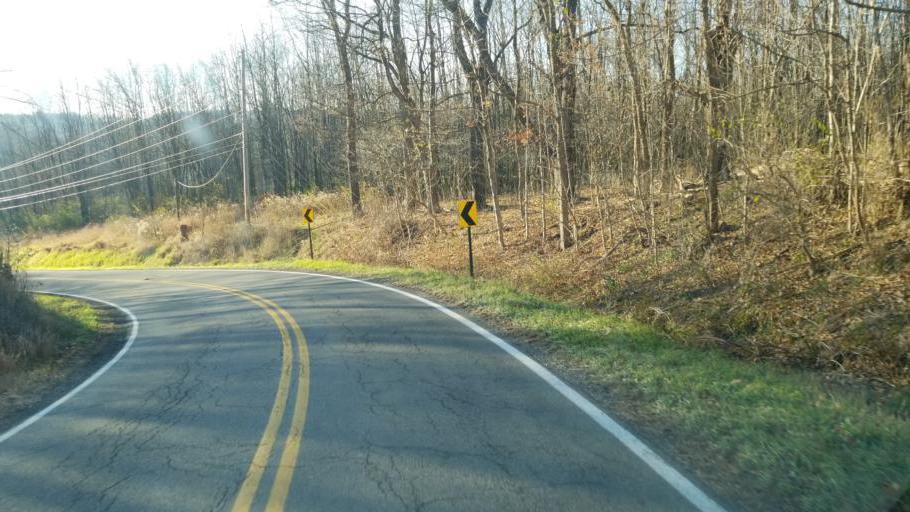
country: US
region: Ohio
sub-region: Medina County
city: Lodi
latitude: 40.9120
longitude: -82.0032
